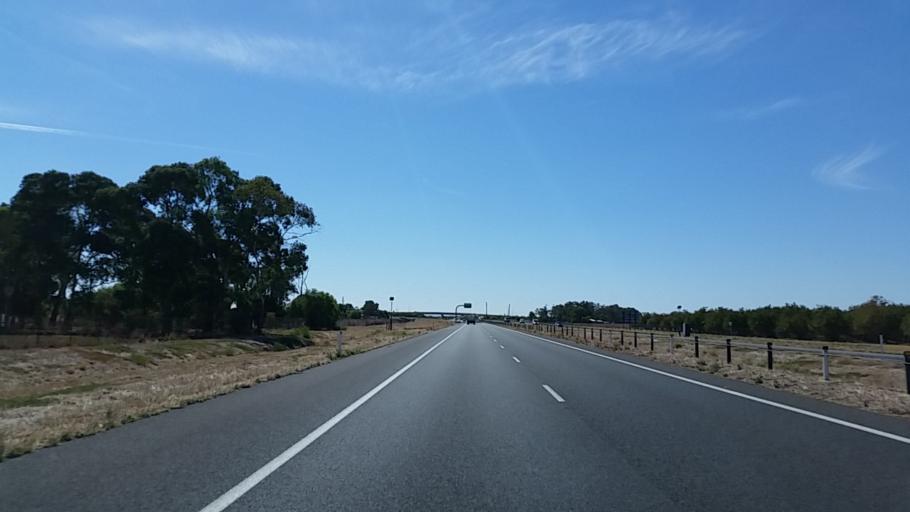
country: AU
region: South Australia
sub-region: Playford
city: Angle Vale
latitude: -34.6438
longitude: 138.6667
